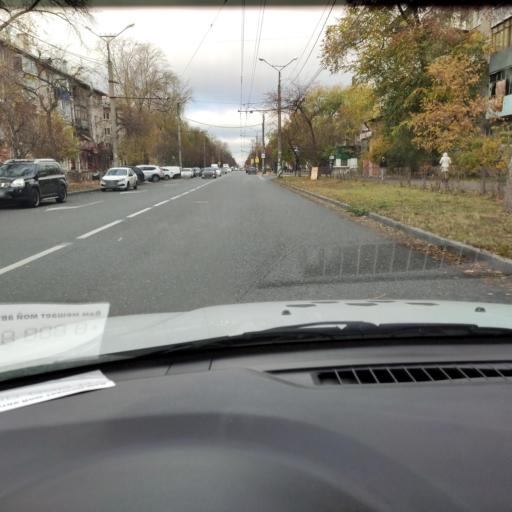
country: RU
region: Samara
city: Tol'yatti
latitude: 53.5118
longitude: 49.4182
